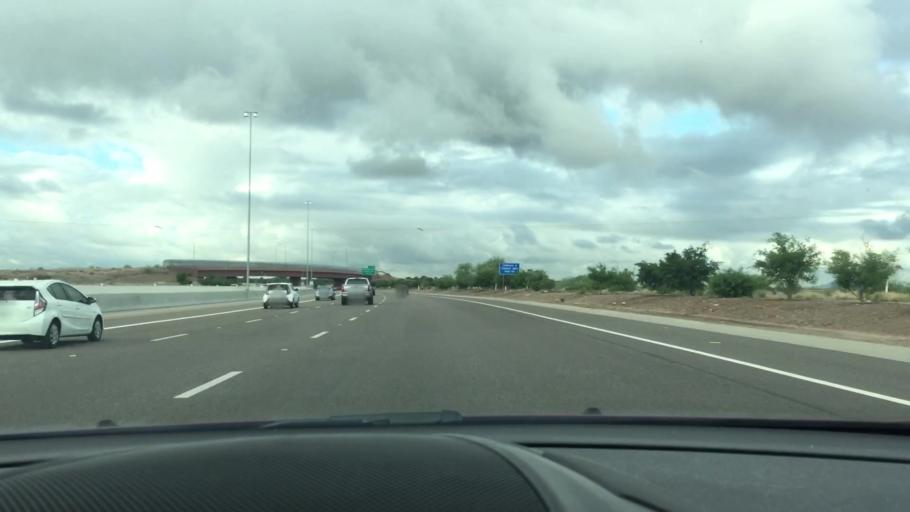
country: US
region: Arizona
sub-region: Maricopa County
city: Mesa
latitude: 33.4828
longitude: -111.7646
